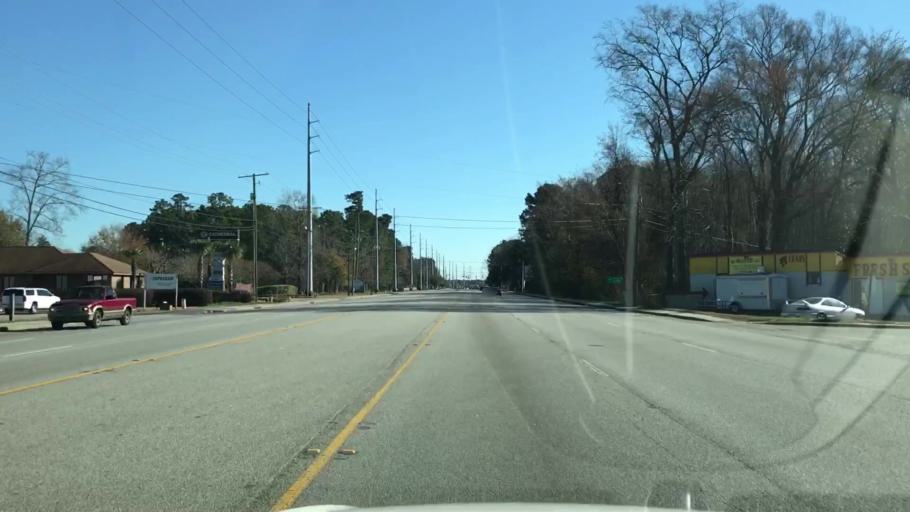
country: US
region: South Carolina
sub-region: Berkeley County
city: Ladson
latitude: 32.9228
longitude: -80.0931
